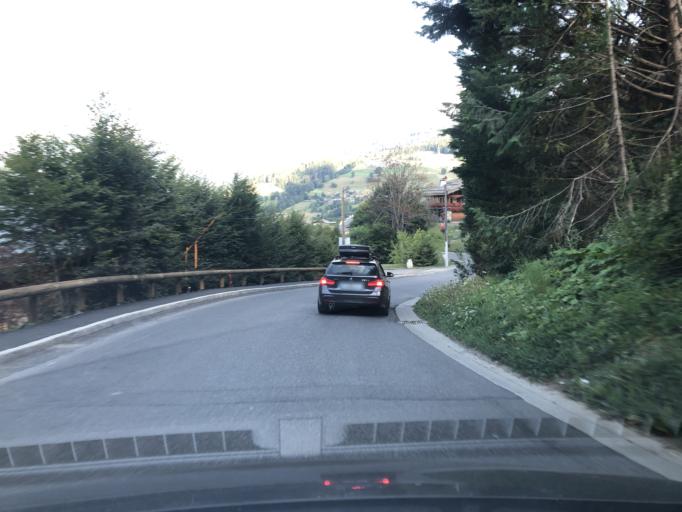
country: FR
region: Rhone-Alpes
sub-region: Departement de la Haute-Savoie
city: Combloux
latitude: 45.8952
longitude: 6.6356
